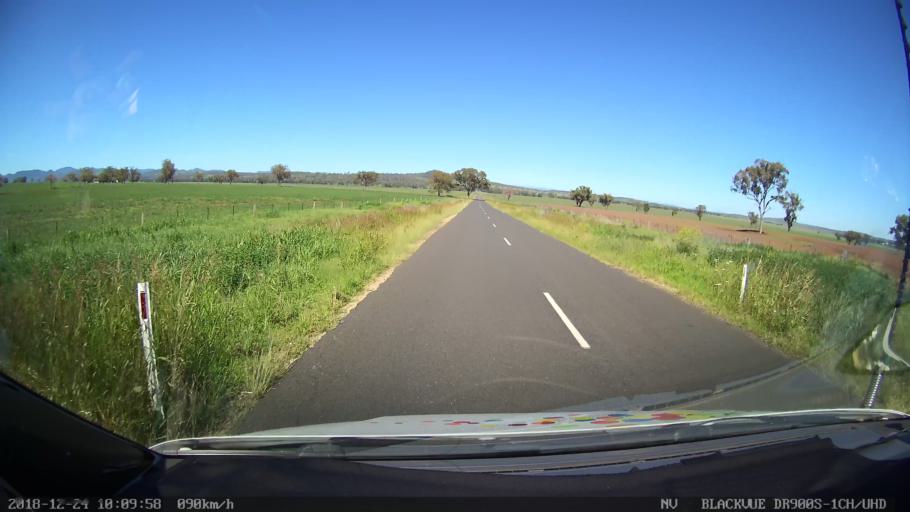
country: AU
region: New South Wales
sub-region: Liverpool Plains
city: Quirindi
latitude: -31.6659
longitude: 150.6827
